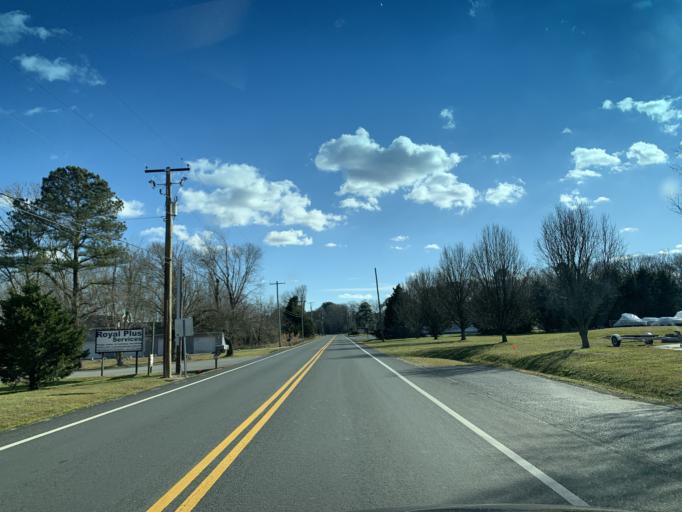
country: US
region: Maryland
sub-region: Worcester County
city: Berlin
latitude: 38.3645
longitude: -75.2014
